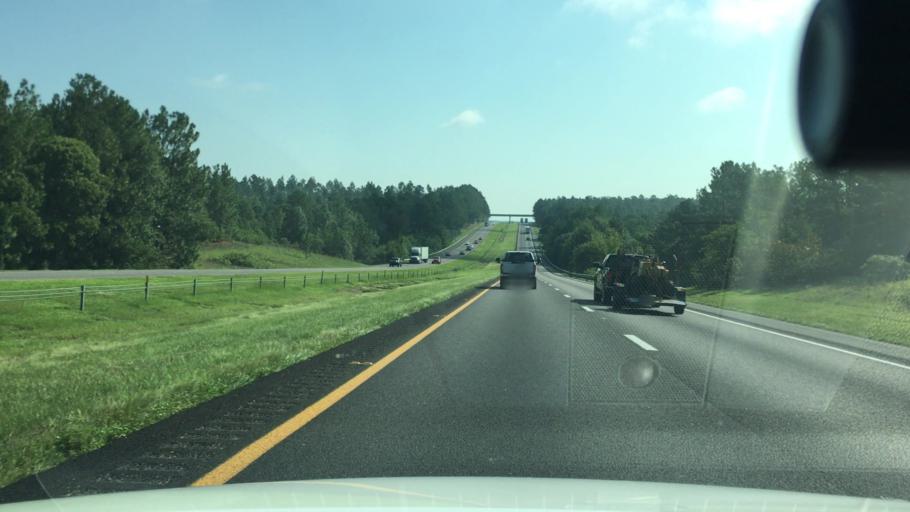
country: US
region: South Carolina
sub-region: Aiken County
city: Graniteville
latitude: 33.6155
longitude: -81.8309
